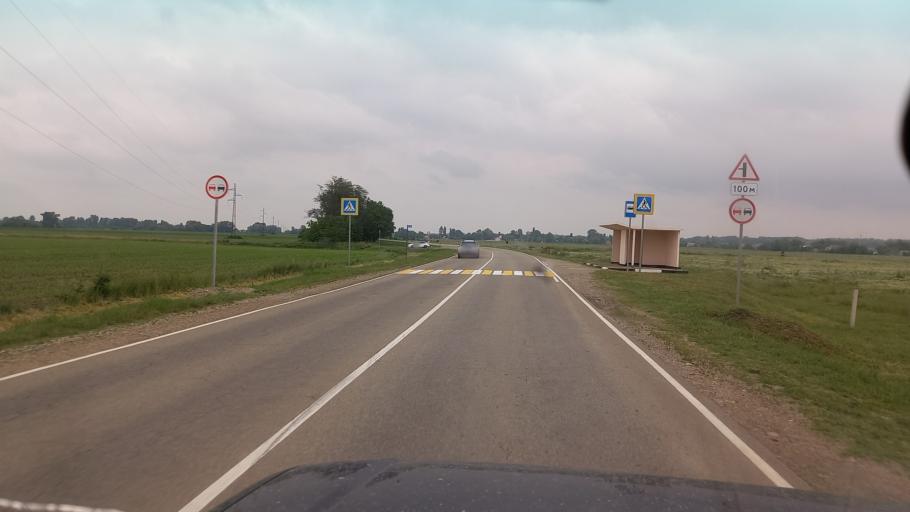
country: RU
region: Krasnodarskiy
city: Labinsk
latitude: 44.6023
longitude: 40.7125
